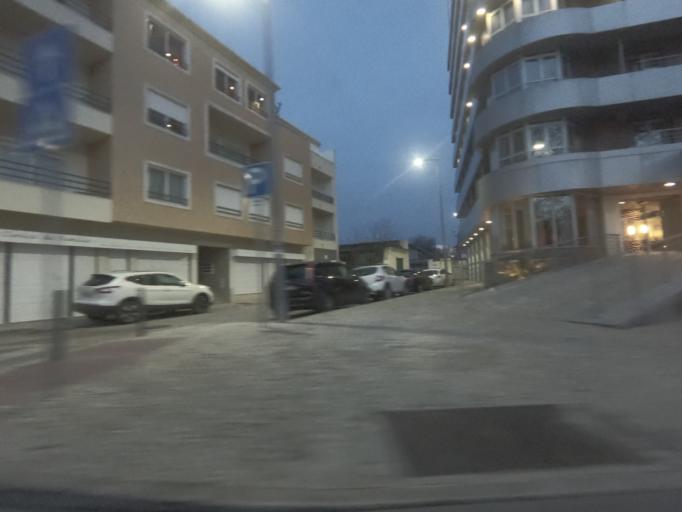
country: PT
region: Setubal
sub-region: Setubal
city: Setubal
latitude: 38.5288
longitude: -8.8899
